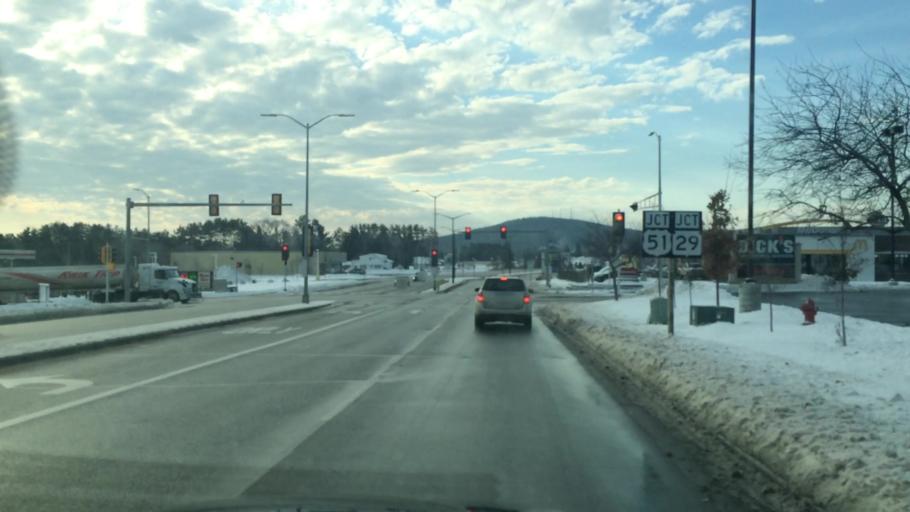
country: US
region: Wisconsin
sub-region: Marathon County
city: Rib Mountain
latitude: 44.9150
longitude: -89.6496
